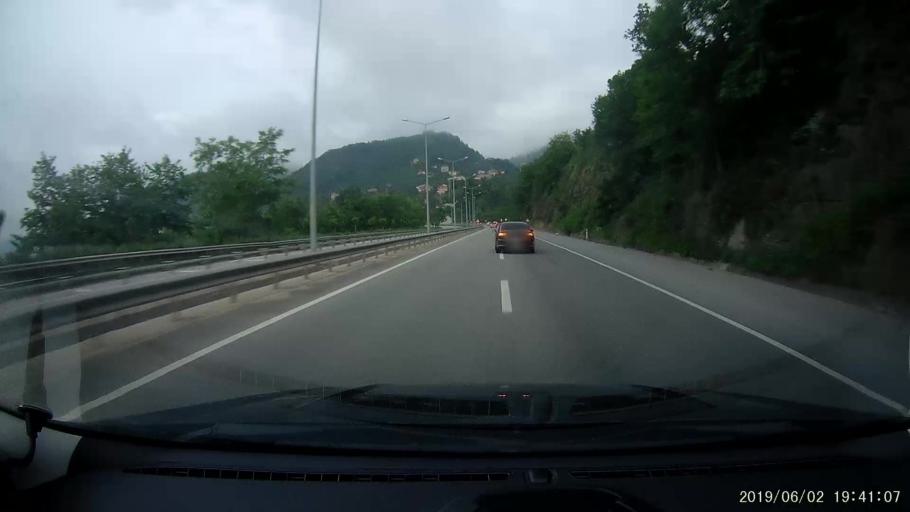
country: TR
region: Giresun
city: Kesap
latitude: 40.9166
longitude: 38.4742
